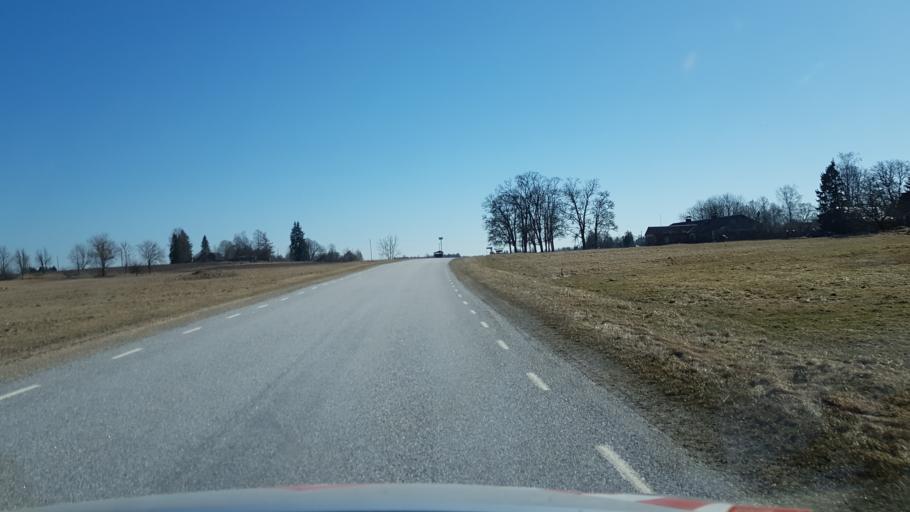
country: EE
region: Jaervamaa
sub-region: Koeru vald
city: Koeru
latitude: 59.0402
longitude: 26.0916
